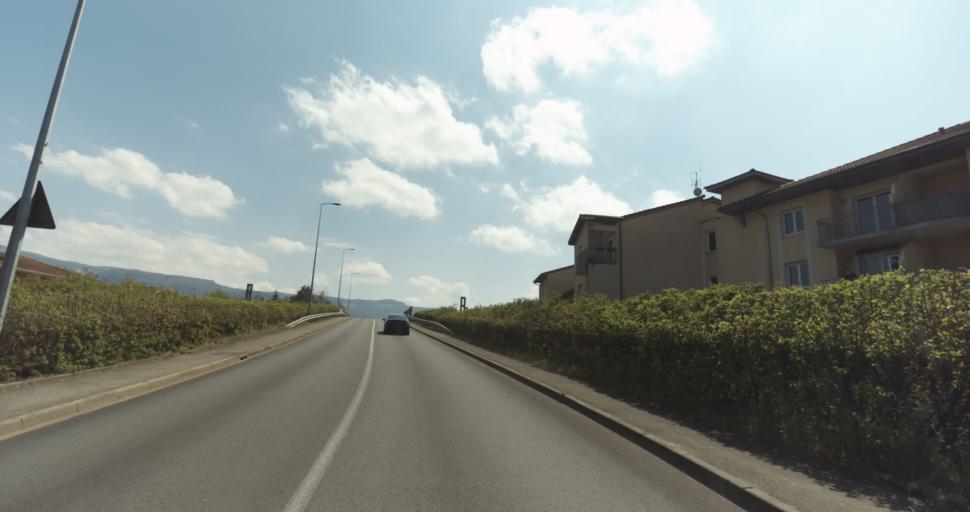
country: FR
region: Rhone-Alpes
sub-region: Departement de l'Isere
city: Saint-Marcellin
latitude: 45.1490
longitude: 5.3172
